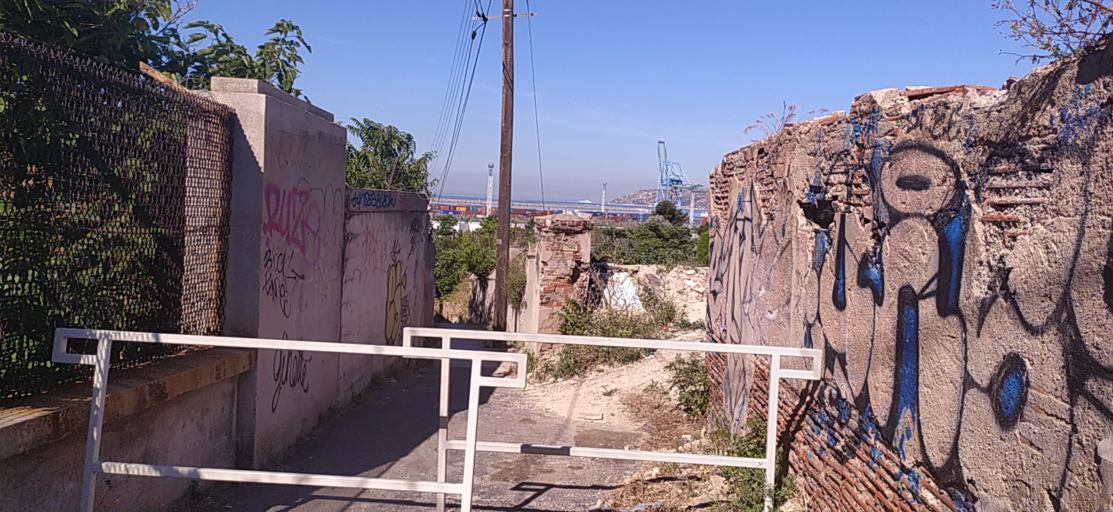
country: FR
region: Provence-Alpes-Cote d'Azur
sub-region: Departement des Bouches-du-Rhone
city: Marseille 16
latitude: 43.3517
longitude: 5.3426
